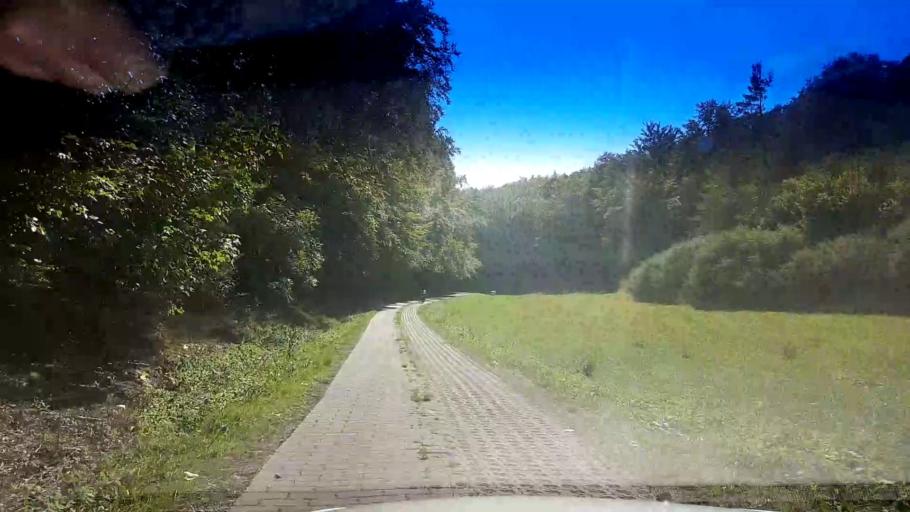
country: DE
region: Bavaria
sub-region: Upper Franconia
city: Poxdorf
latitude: 49.8889
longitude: 11.0813
